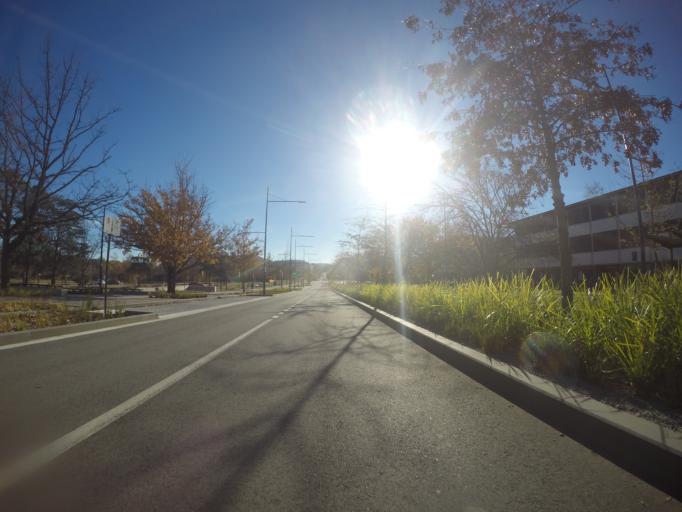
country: AU
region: Australian Capital Territory
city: Canberra
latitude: -35.2868
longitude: 149.1369
